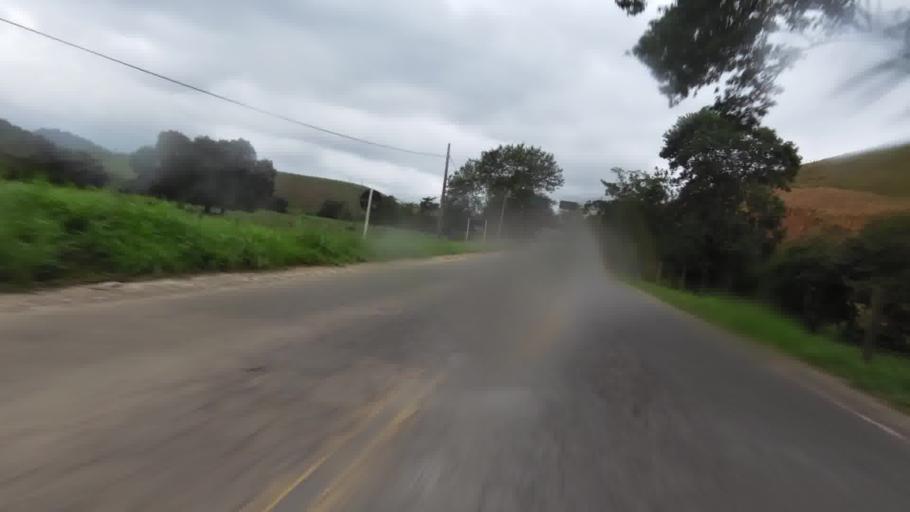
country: BR
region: Espirito Santo
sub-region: Alfredo Chaves
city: Alfredo Chaves
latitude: -20.6579
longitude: -40.7482
